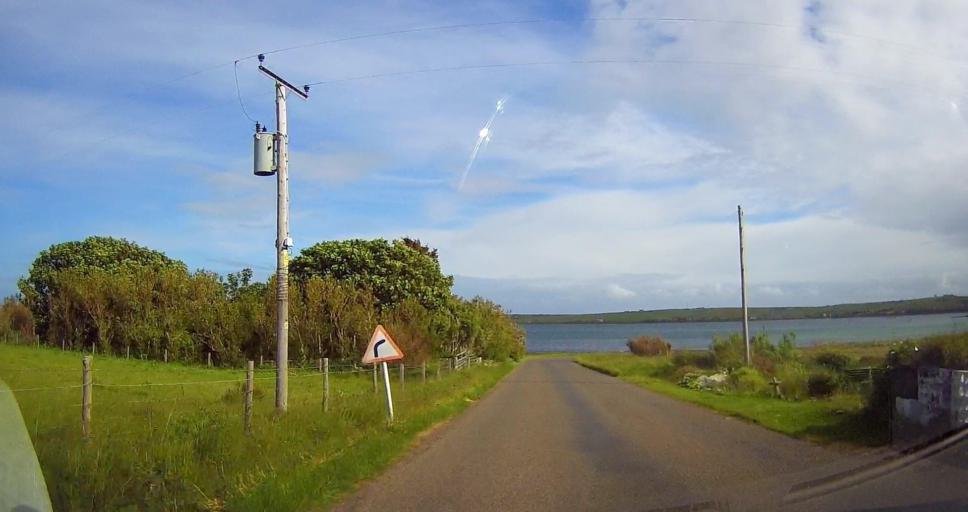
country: GB
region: Scotland
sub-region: Orkney Islands
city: Stromness
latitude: 58.8126
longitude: -3.2007
